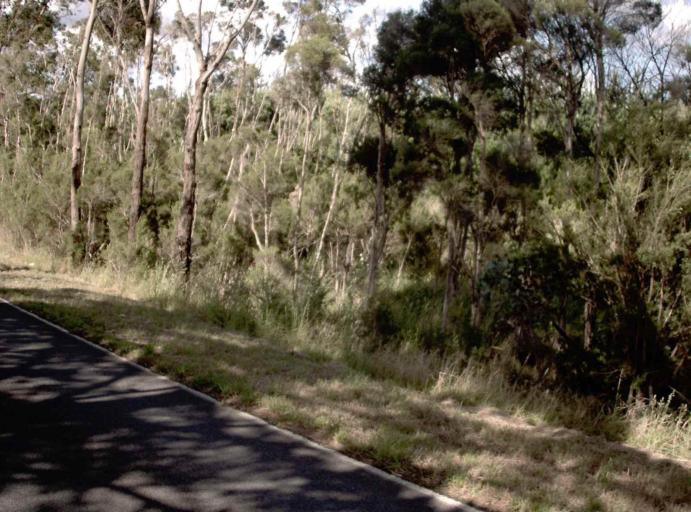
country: AU
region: Victoria
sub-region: Latrobe
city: Morwell
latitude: -38.1779
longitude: 146.4051
